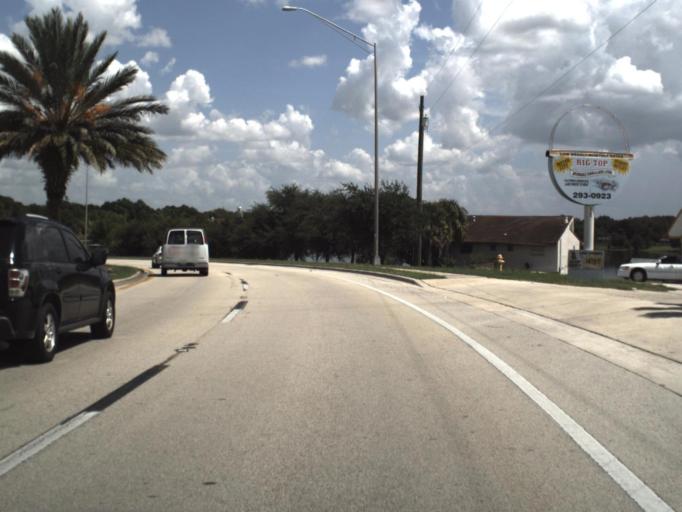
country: US
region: Florida
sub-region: Polk County
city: Cypress Gardens
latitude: 28.0040
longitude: -81.7095
